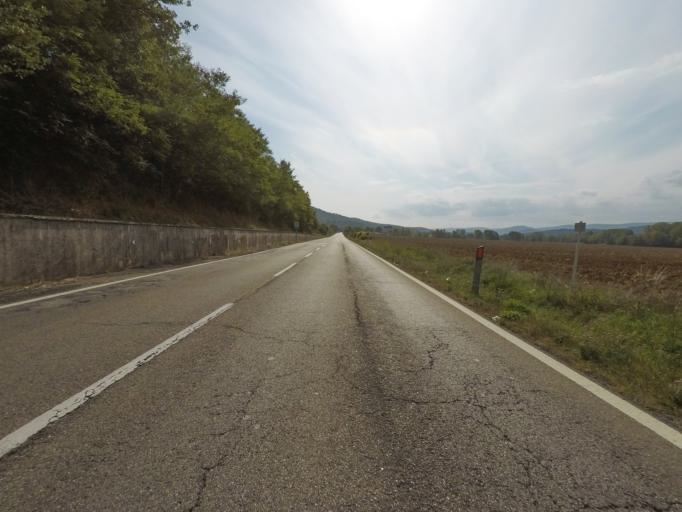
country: IT
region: Tuscany
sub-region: Provincia di Siena
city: Rosia
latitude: 43.2153
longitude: 11.2767
